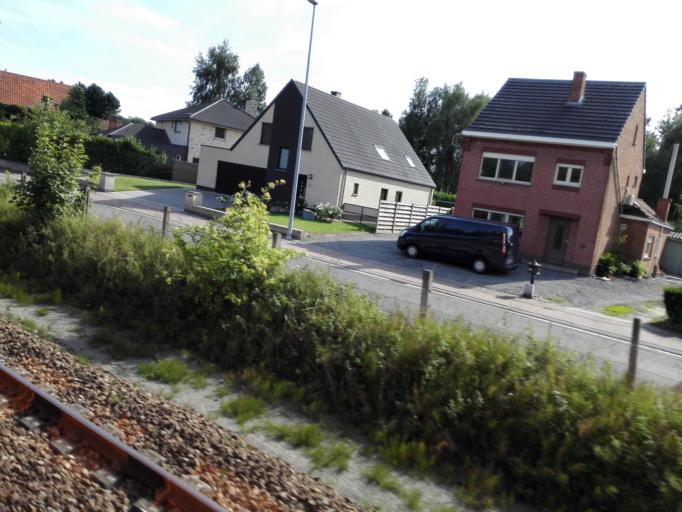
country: BE
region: Flanders
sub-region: Provincie Vlaams-Brabant
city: Boortmeerbeek
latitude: 50.9736
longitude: 4.5933
